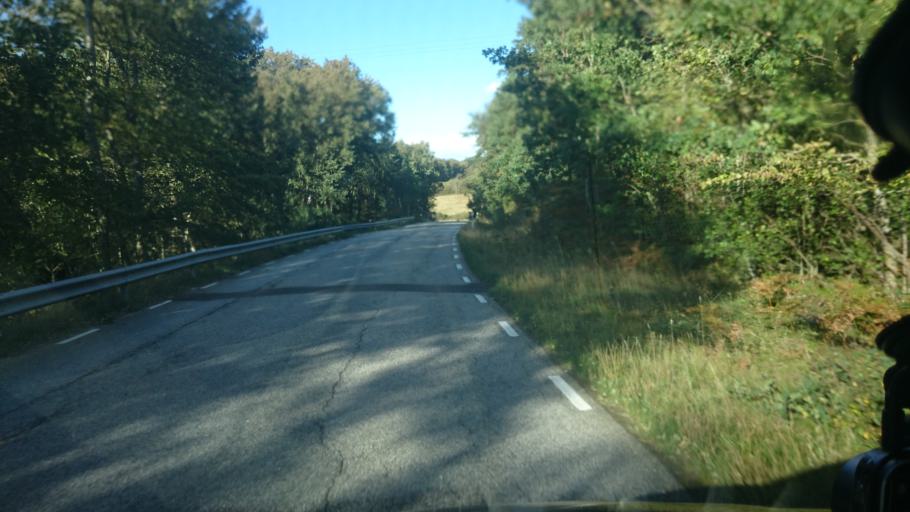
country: SE
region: Vaestra Goetaland
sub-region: Lysekils Kommun
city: Lysekil
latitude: 58.3330
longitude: 11.4280
